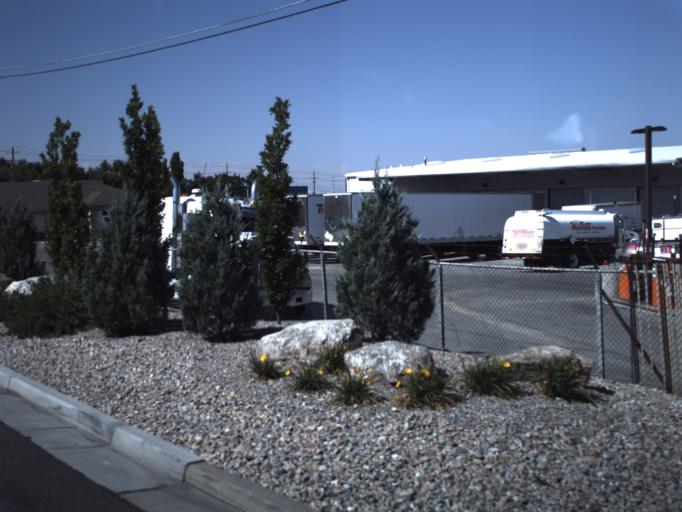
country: US
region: Utah
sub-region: Davis County
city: Woods Cross
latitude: 40.8626
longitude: -111.9028
